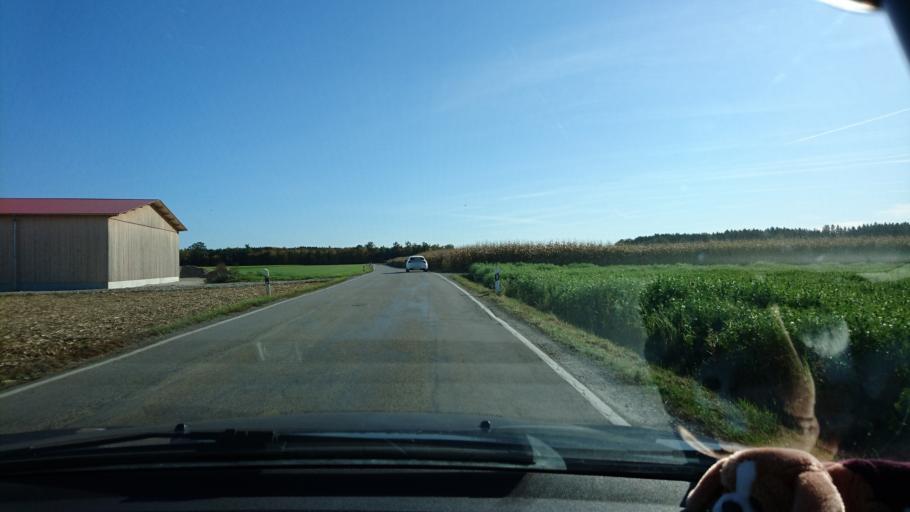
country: DE
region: Bavaria
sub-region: Upper Bavaria
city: Anzing
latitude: 48.1248
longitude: 11.8319
